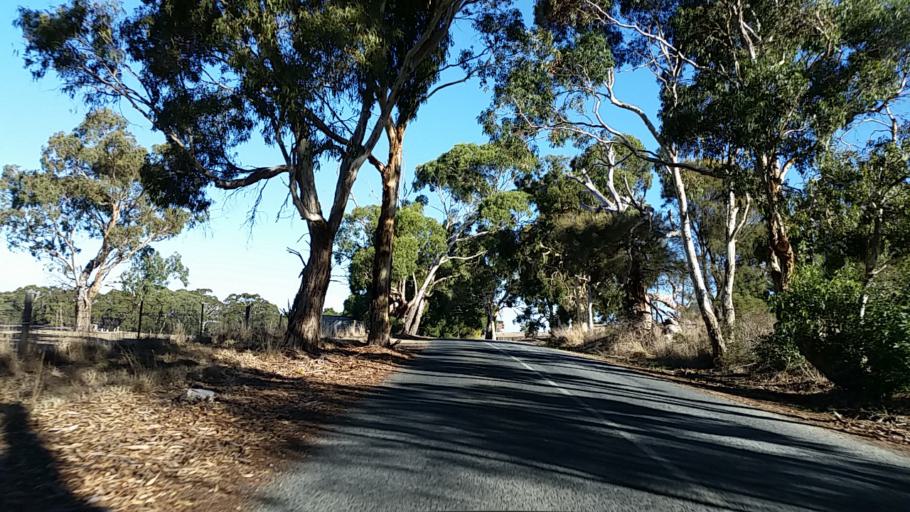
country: AU
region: South Australia
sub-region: Mount Barker
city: Nairne
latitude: -35.0593
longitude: 138.9250
